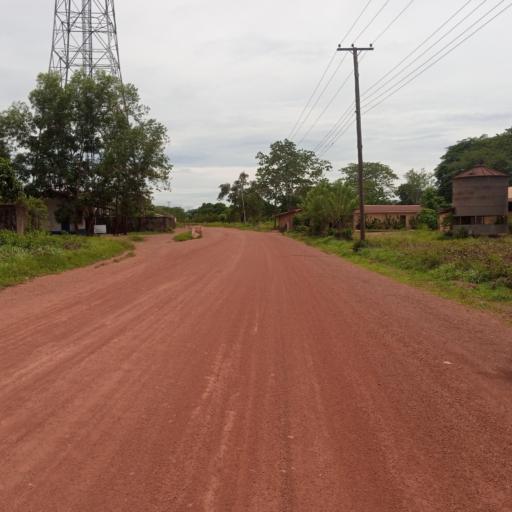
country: SL
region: Southern Province
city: Largo
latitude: 8.1124
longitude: -12.0740
